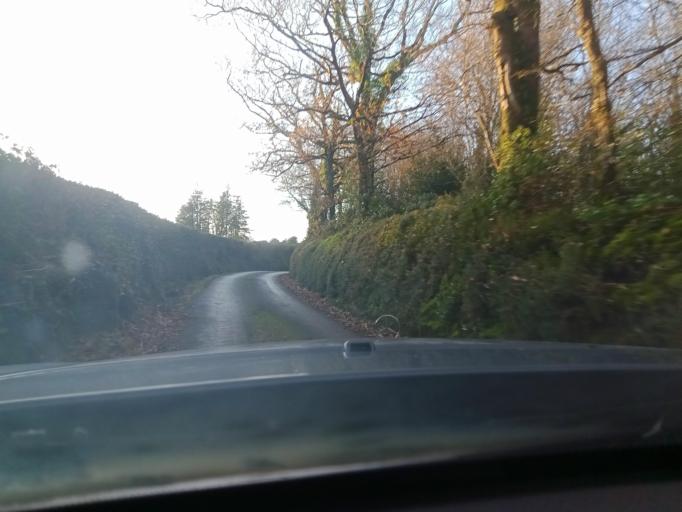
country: IE
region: Leinster
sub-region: Kilkenny
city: Graiguenamanagh
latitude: 52.4831
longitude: -6.9504
